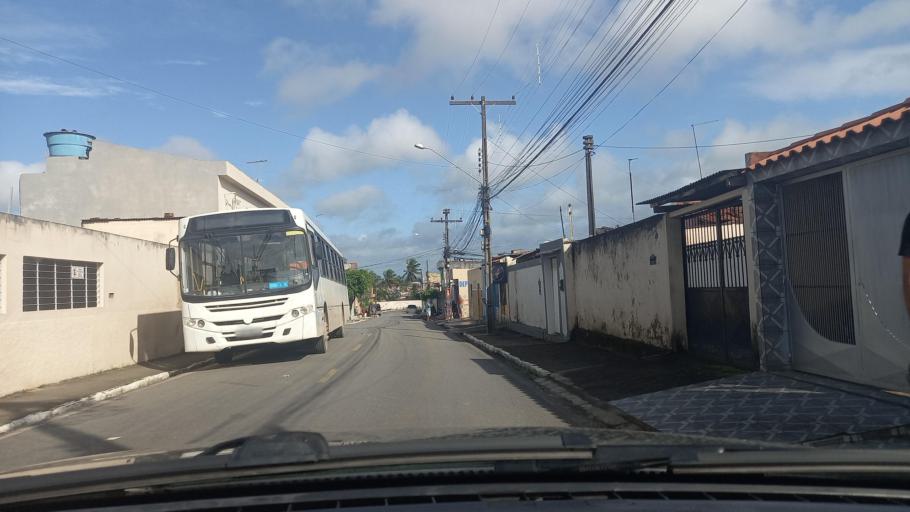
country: BR
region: Pernambuco
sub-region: Vitoria De Santo Antao
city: Vitoria de Santo Antao
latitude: -8.1184
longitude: -35.2803
